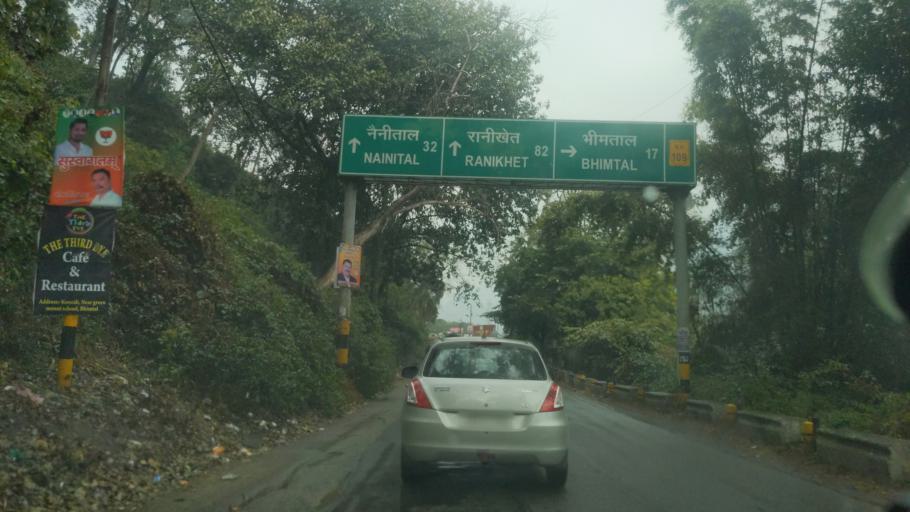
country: IN
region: Uttarakhand
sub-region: Naini Tal
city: Bhim Tal
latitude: 29.2894
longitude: 79.5465
